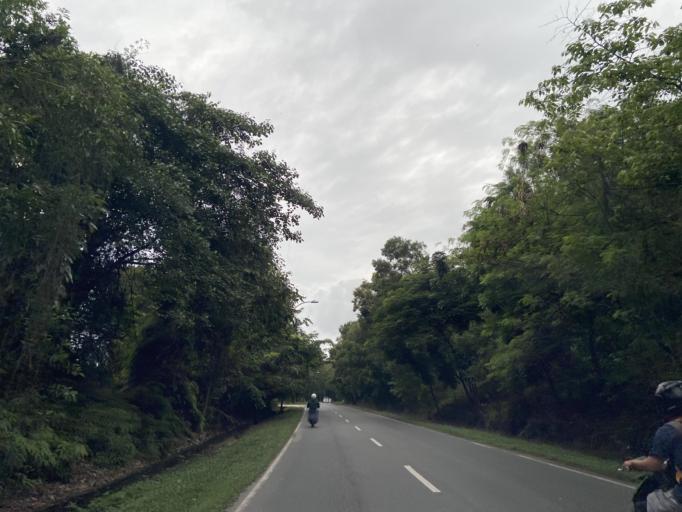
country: SG
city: Singapore
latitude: 1.1195
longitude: 104.0146
